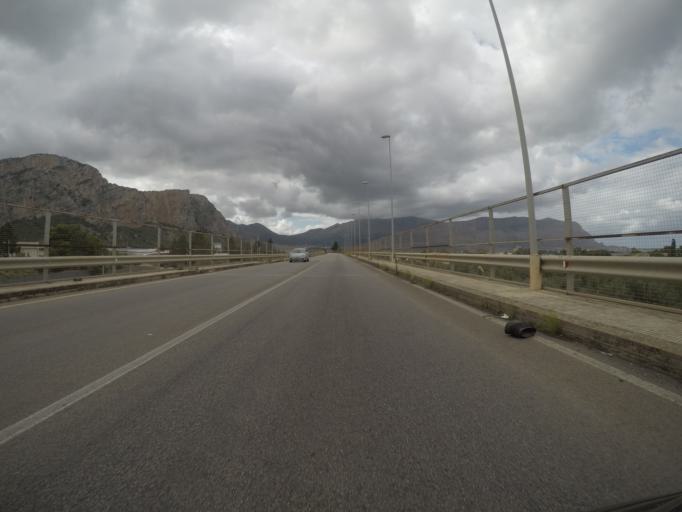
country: IT
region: Sicily
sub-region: Palermo
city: Capaci
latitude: 38.1658
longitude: 13.2214
